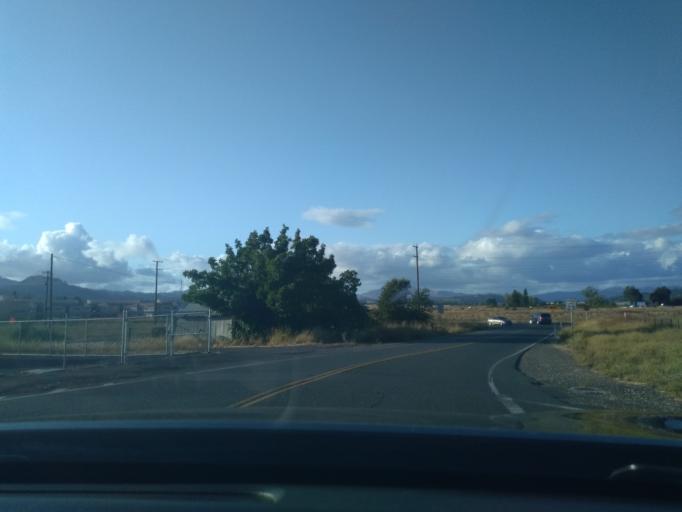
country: US
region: California
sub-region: Mendocino County
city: Ukiah
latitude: 39.1586
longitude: -123.2000
